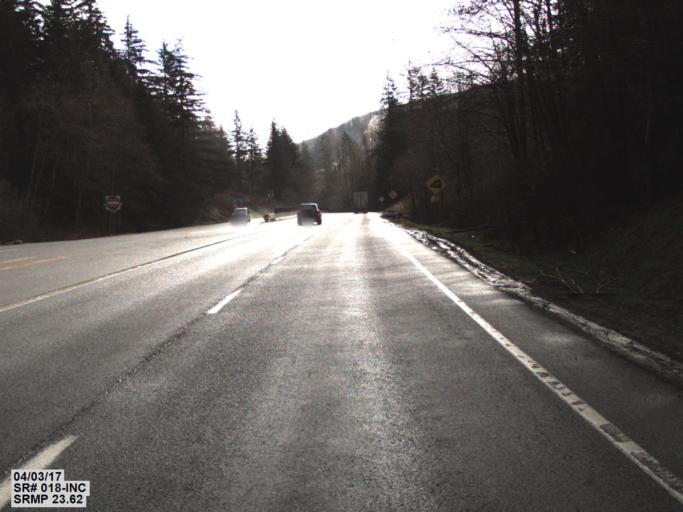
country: US
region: Washington
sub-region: King County
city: Hobart
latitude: 47.4660
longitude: -121.9306
